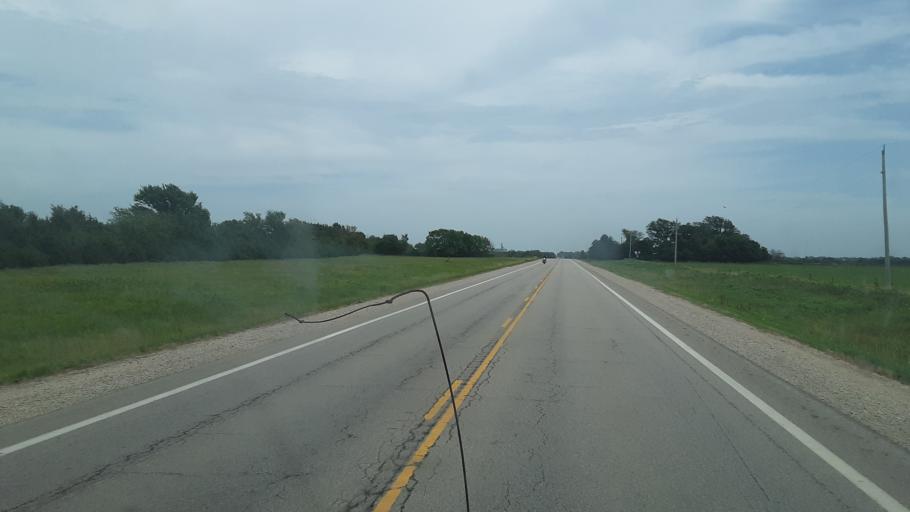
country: US
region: Kansas
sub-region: Woodson County
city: Yates Center
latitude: 37.8796
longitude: -95.7647
